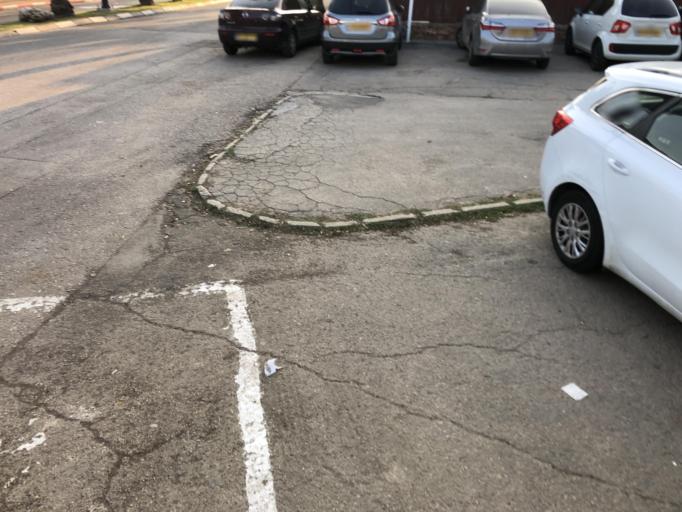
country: IL
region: Northern District
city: `Akko
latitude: 32.9270
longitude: 35.0872
